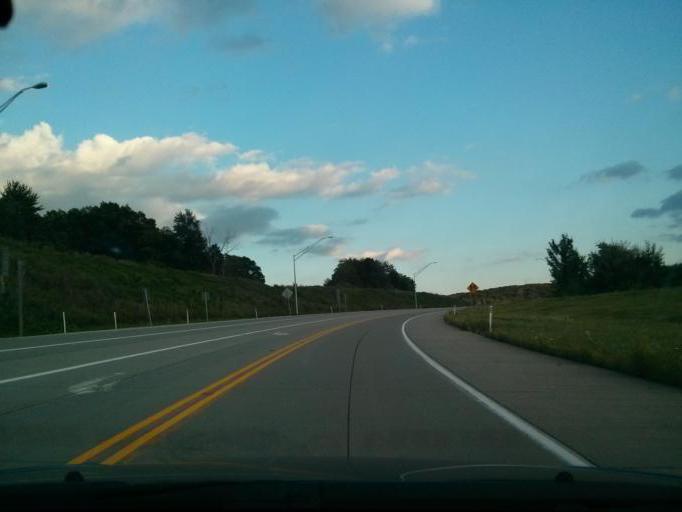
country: US
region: Pennsylvania
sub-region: Centre County
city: Park Forest Village
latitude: 40.8215
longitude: -77.9406
